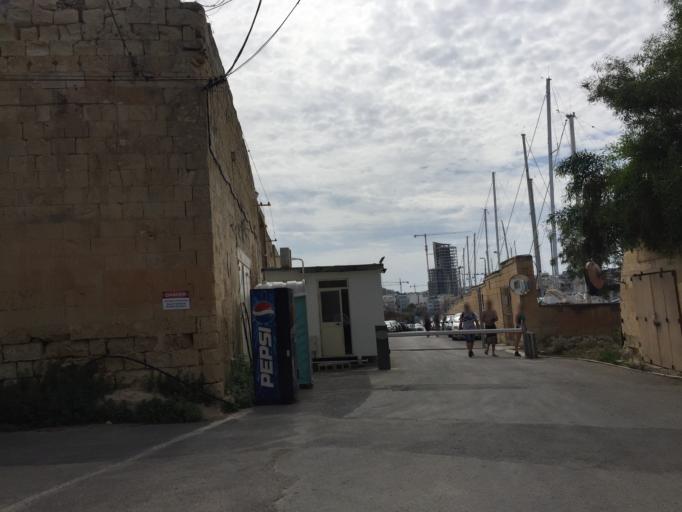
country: MT
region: Tas-Sliema
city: Sliema
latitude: 35.9047
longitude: 14.5020
